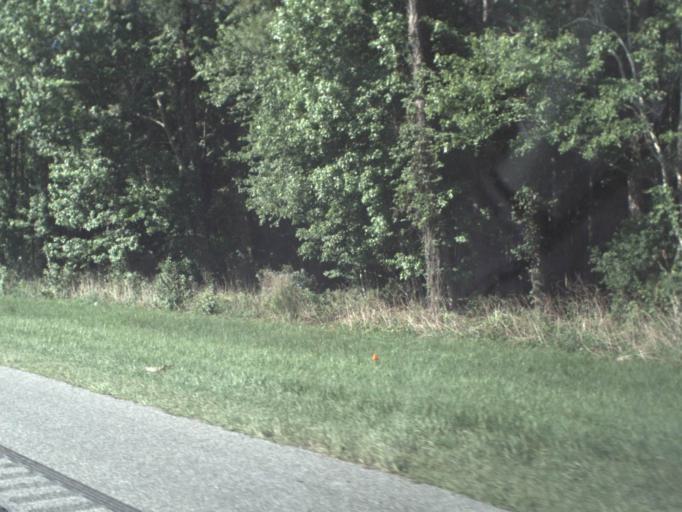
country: US
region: Florida
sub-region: Saint Johns County
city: Palm Valley
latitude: 30.0132
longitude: -81.4784
